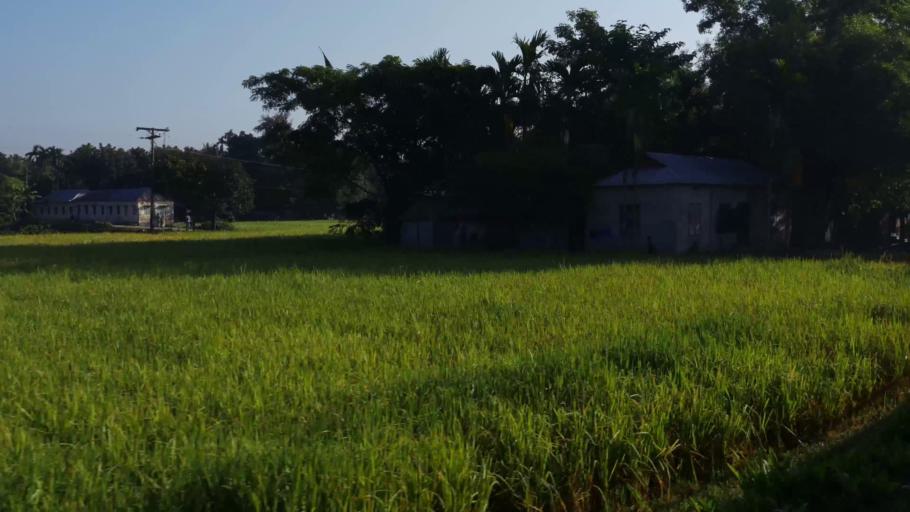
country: BD
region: Dhaka
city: Jamalpur
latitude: 24.8633
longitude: 90.0964
